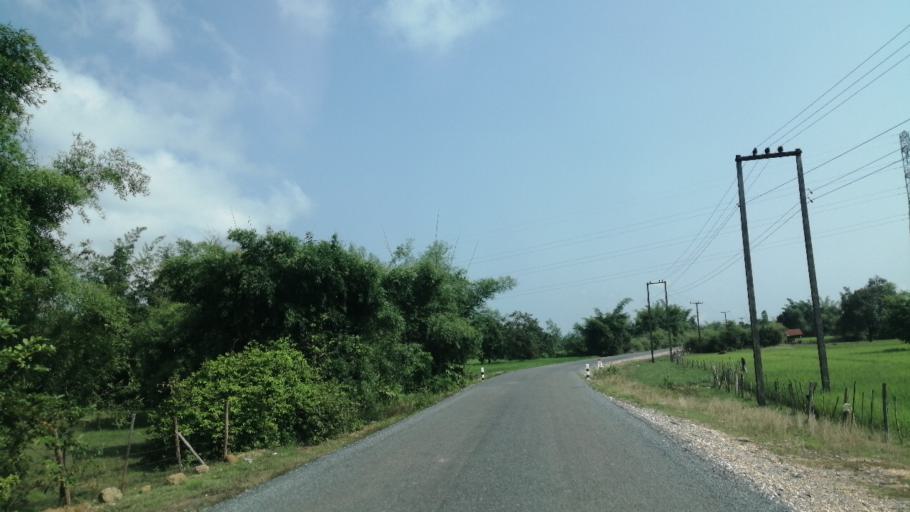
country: TH
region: Changwat Bueng Kan
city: Bung Khla
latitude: 18.3345
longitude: 103.8600
